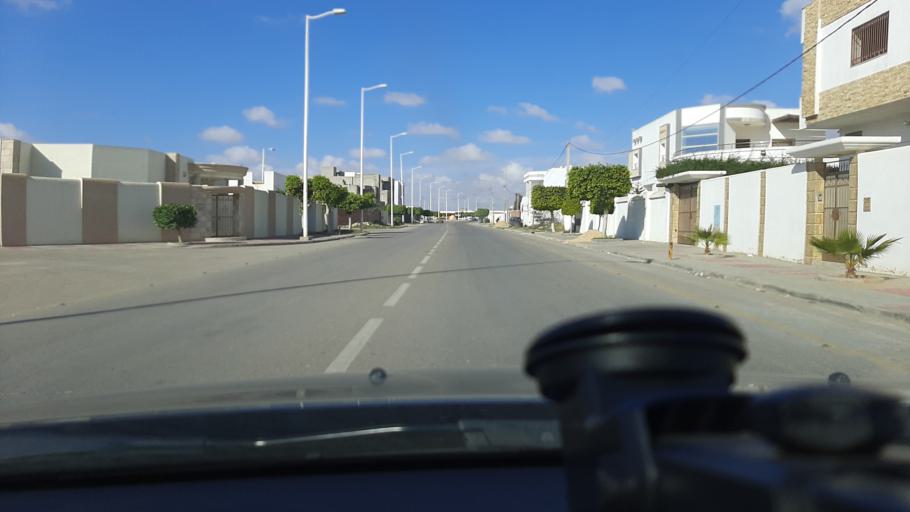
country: TN
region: Safaqis
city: Sfax
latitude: 34.8086
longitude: 10.7120
